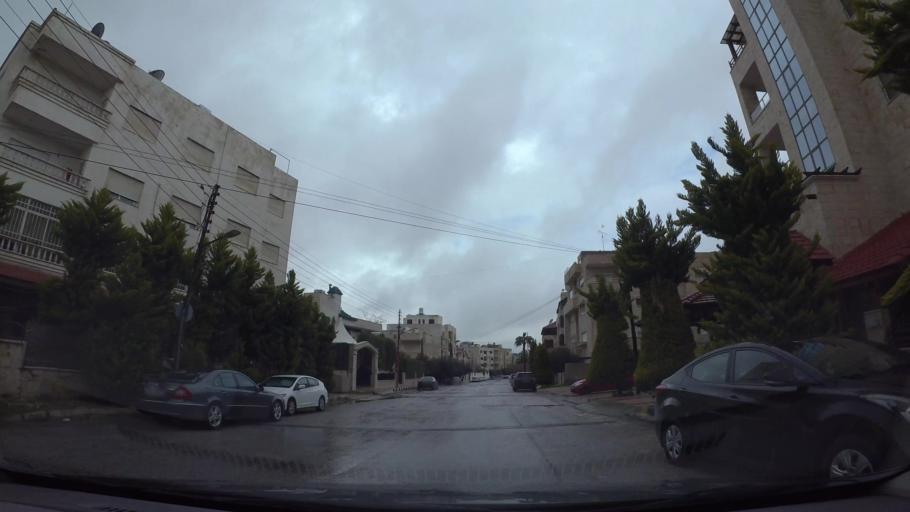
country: JO
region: Amman
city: Wadi as Sir
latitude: 31.9670
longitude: 35.8634
